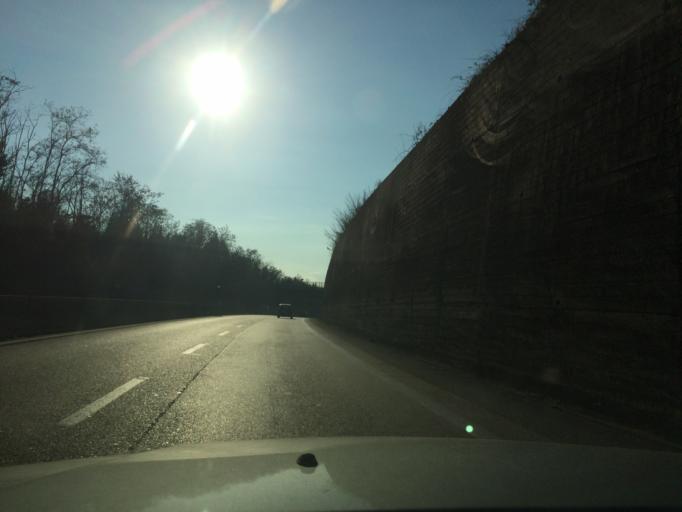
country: IT
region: Umbria
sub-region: Provincia di Terni
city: Fornole
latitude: 42.5344
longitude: 12.4794
